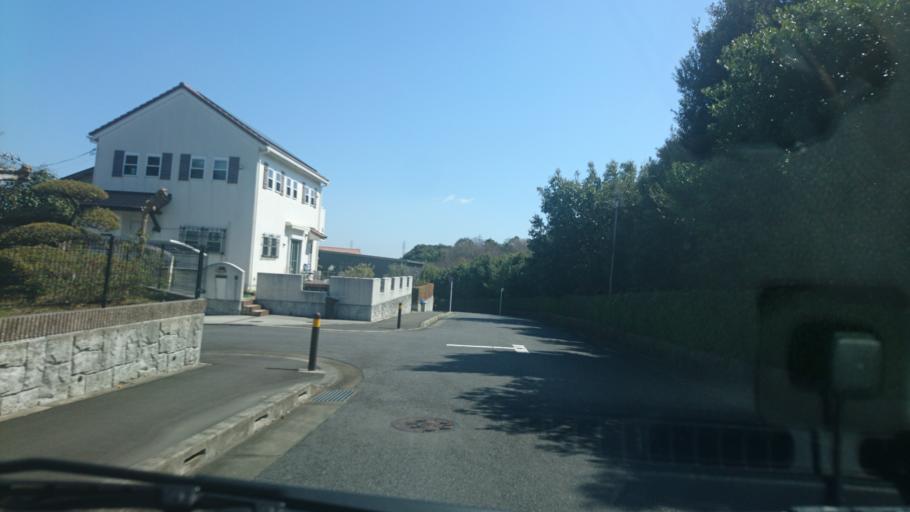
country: JP
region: Kanagawa
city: Fujisawa
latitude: 35.3893
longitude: 139.4289
